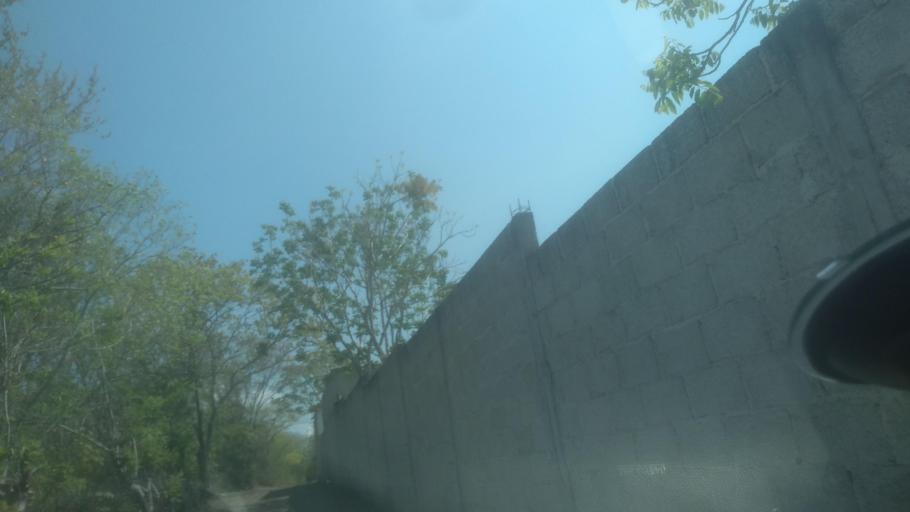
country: MX
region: Veracruz
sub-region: Emiliano Zapata
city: Plan del Rio
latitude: 19.3929
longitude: -96.6296
